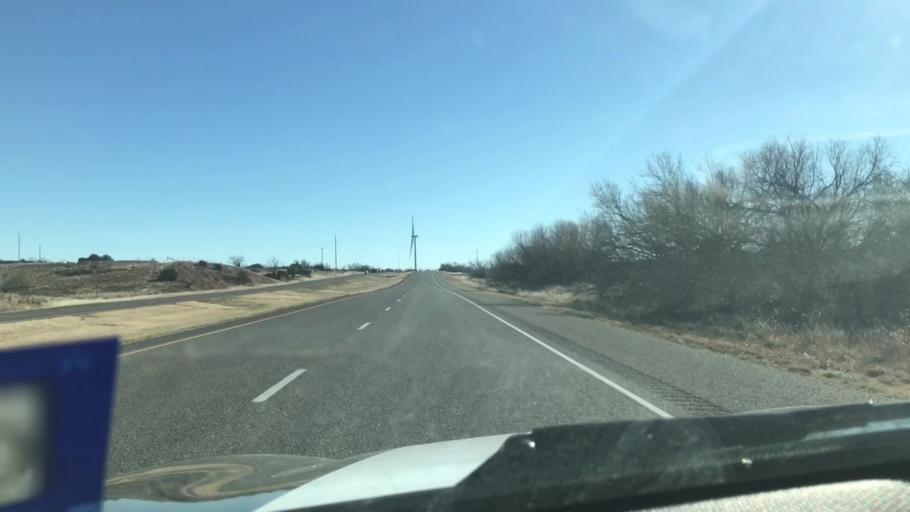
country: US
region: Texas
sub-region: Scurry County
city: Snyder
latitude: 32.8917
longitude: -101.0545
